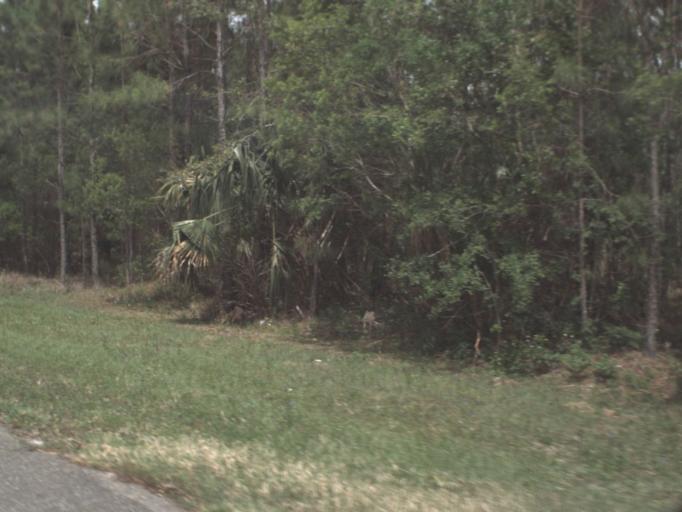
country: US
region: Florida
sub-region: Flagler County
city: Bunnell
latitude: 29.4097
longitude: -81.3054
